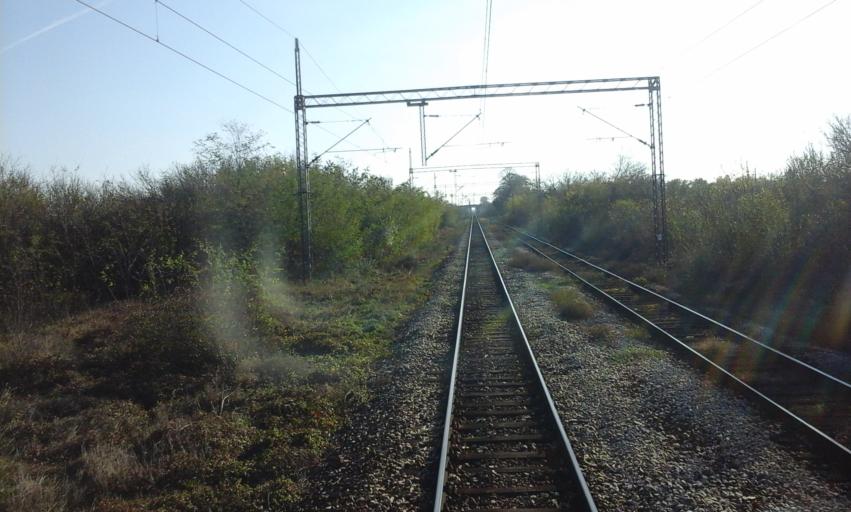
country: RS
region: Autonomna Pokrajina Vojvodina
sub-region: Severnobacki Okrug
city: Mali Igos
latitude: 45.7486
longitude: 19.6488
